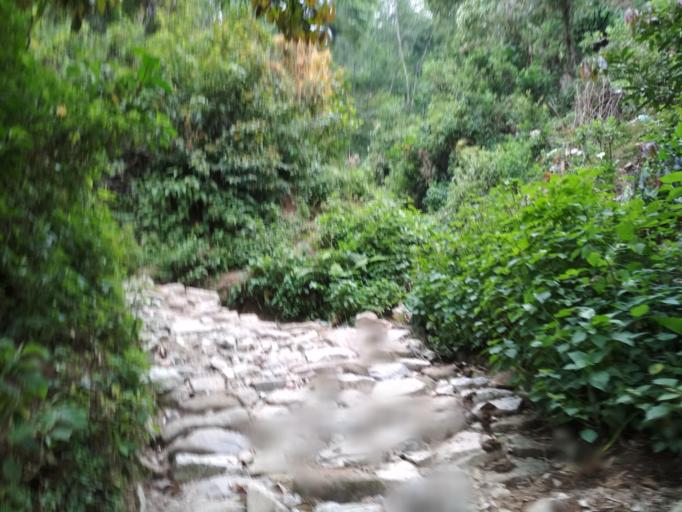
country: MX
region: Veracruz
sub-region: La Perla
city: Metlac Hernandez (Metlac Primero)
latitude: 18.9784
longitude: -97.1355
